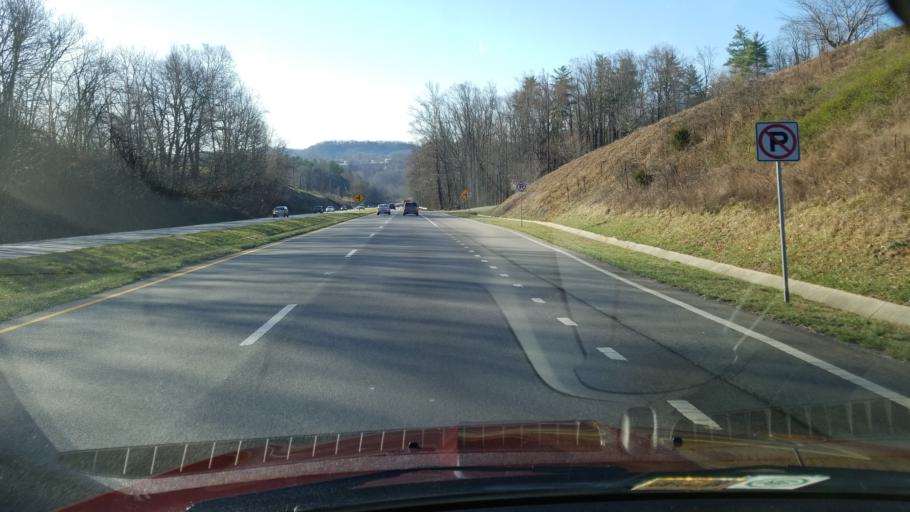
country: US
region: Virginia
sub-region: Franklin County
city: Rocky Mount
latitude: 37.0604
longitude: -79.8844
